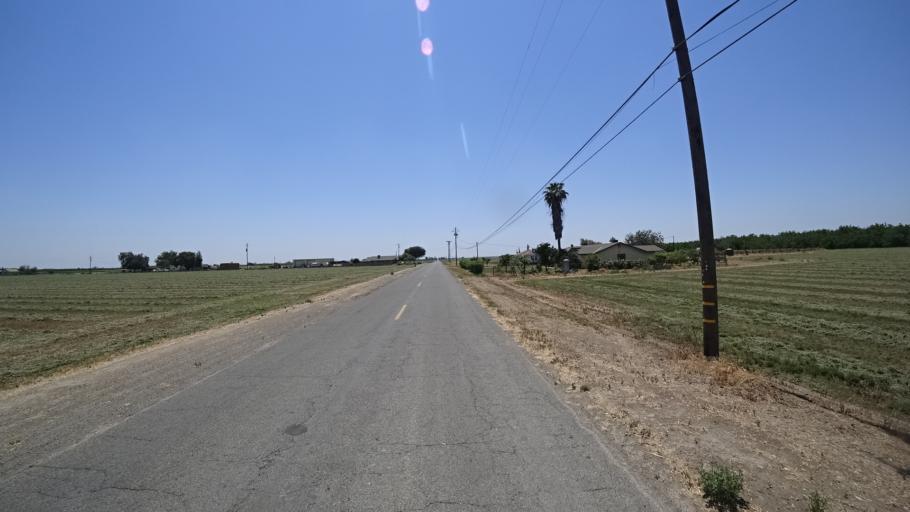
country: US
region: California
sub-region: Kings County
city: Lucerne
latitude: 36.3807
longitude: -119.7270
